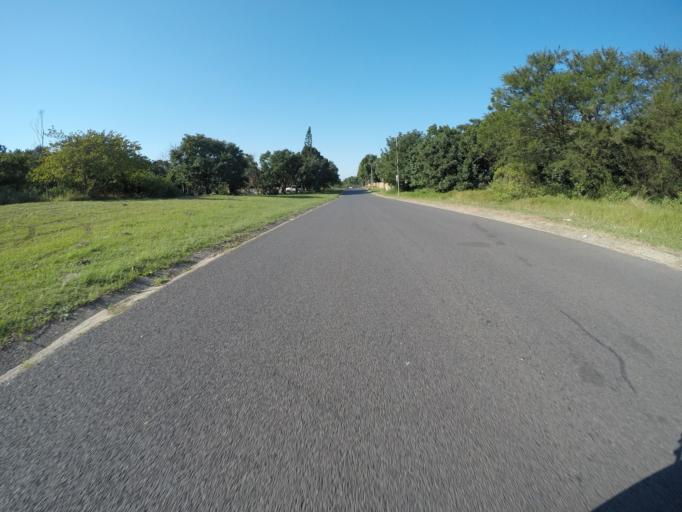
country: ZA
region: KwaZulu-Natal
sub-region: uThungulu District Municipality
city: Richards Bay
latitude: -28.7664
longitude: 32.0572
